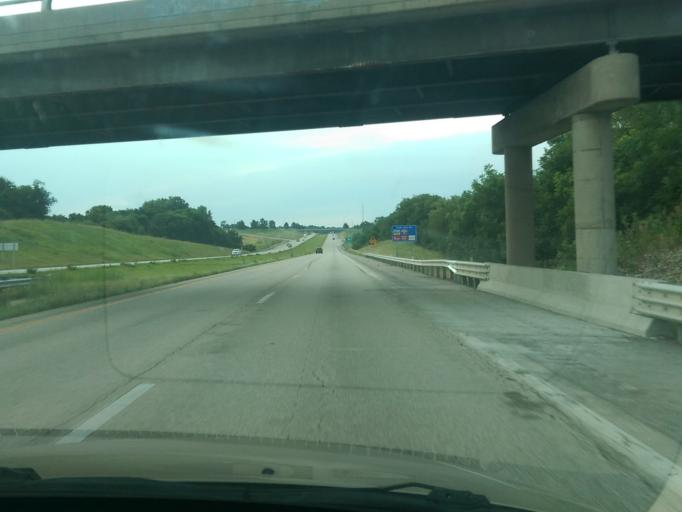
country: US
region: Missouri
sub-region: Andrew County
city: Country Club Village
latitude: 39.8066
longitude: -94.8007
